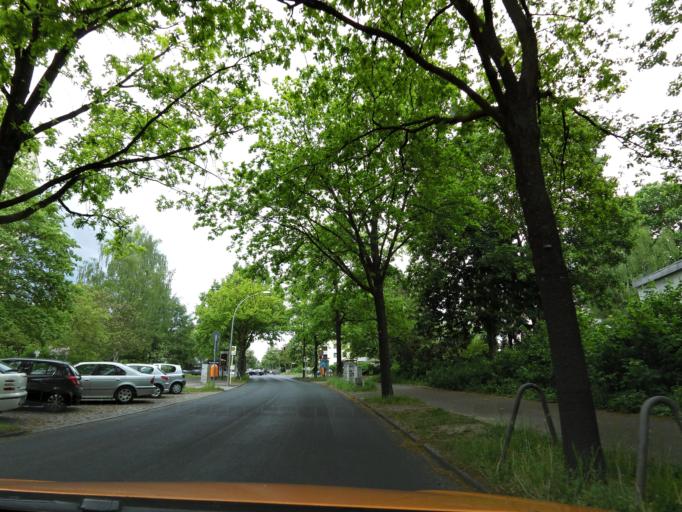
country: DE
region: Berlin
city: Zehlendorf Bezirk
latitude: 52.4186
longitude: 13.2486
